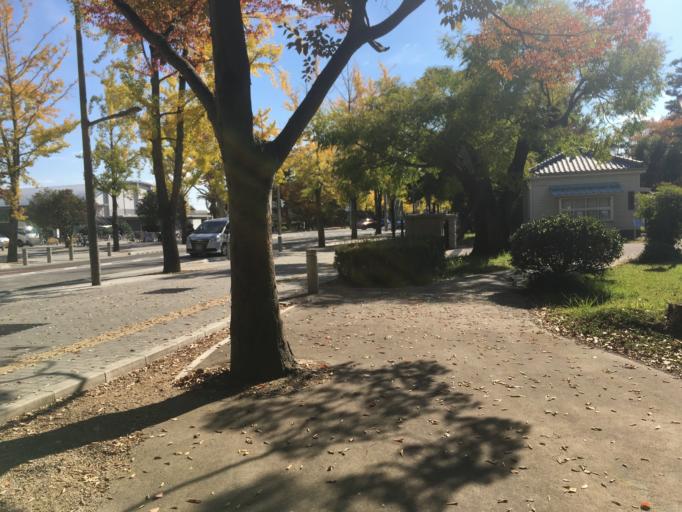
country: JP
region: Okayama
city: Okayama-shi
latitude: 34.6870
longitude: 133.9195
